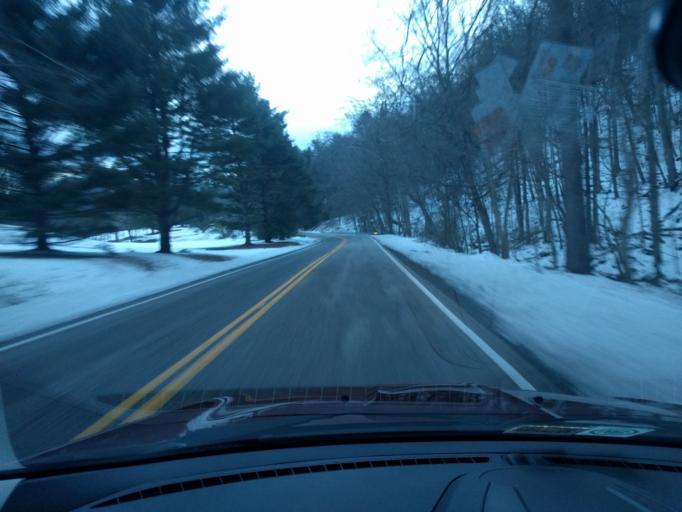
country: US
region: Virginia
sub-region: Bath County
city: Warm Springs
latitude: 37.9467
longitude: -79.8714
